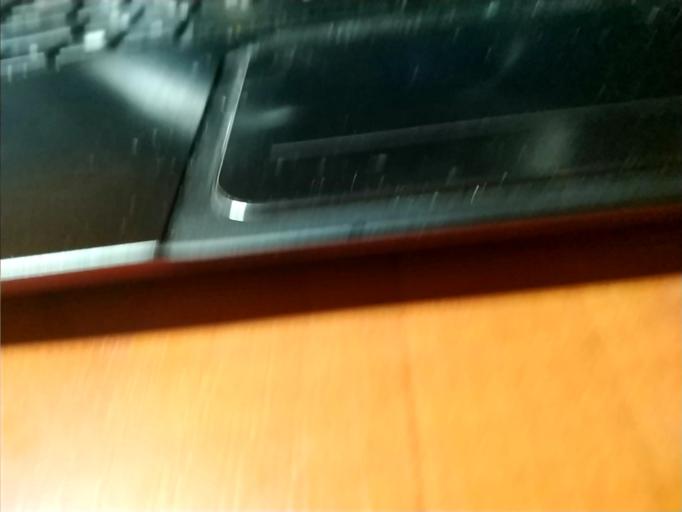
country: RU
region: Tverskaya
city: Ves'yegonsk
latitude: 58.6984
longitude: 37.5439
